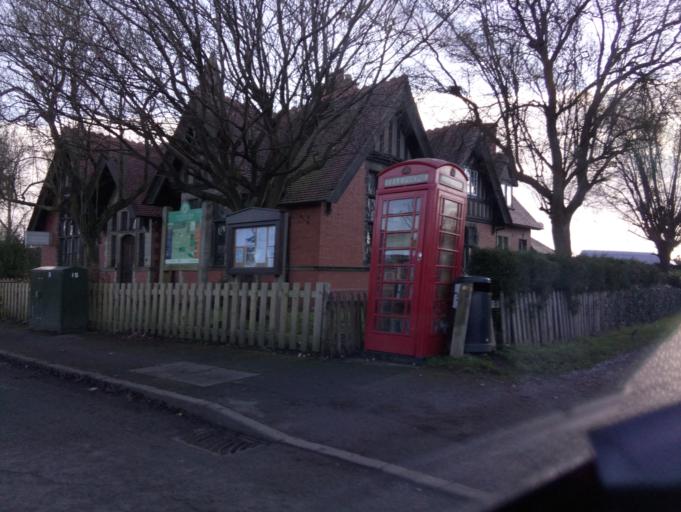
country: GB
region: England
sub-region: Staffordshire
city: Barton under Needwood
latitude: 52.8039
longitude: -1.7311
